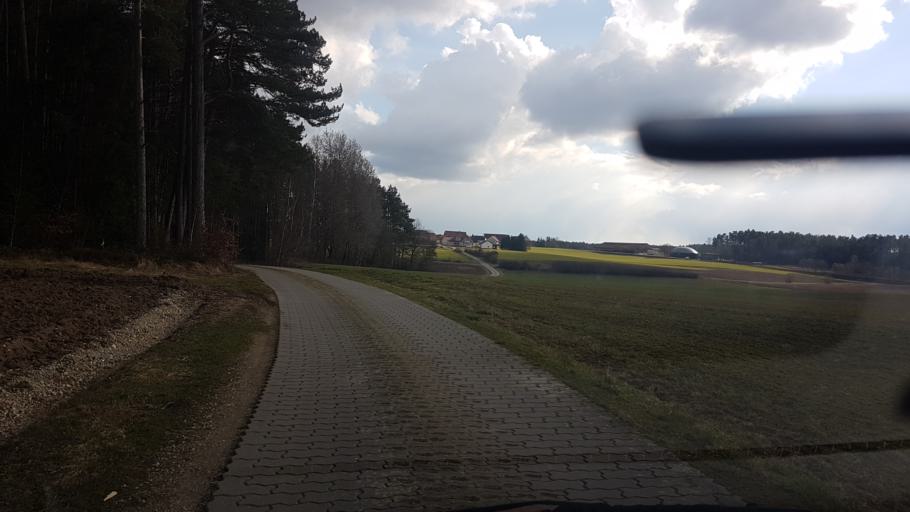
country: DE
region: Bavaria
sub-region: Upper Franconia
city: Stadelhofen
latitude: 49.9942
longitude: 11.2306
